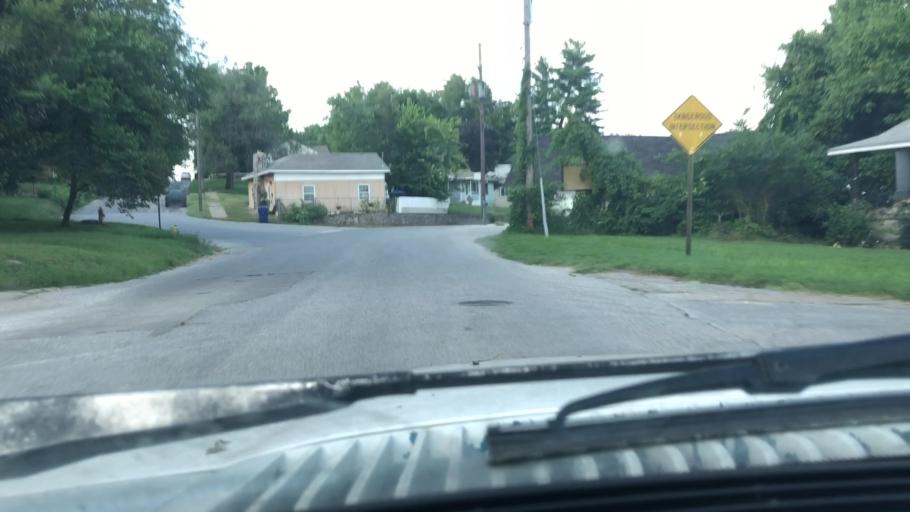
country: US
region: Missouri
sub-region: Newton County
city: Neosho
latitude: 36.8624
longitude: -94.3663
